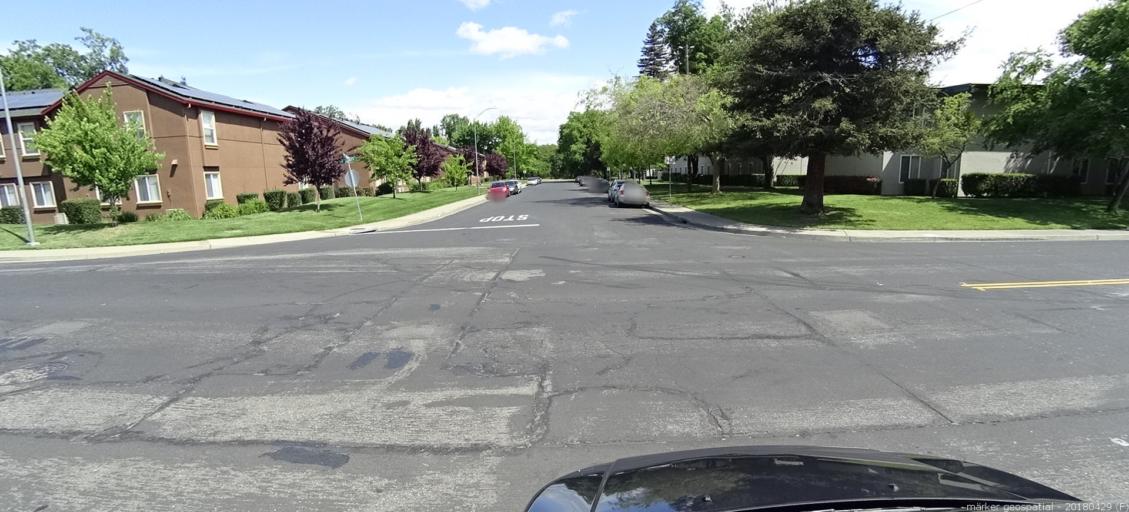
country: US
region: California
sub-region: Yolo County
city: West Sacramento
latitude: 38.5852
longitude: -121.5163
